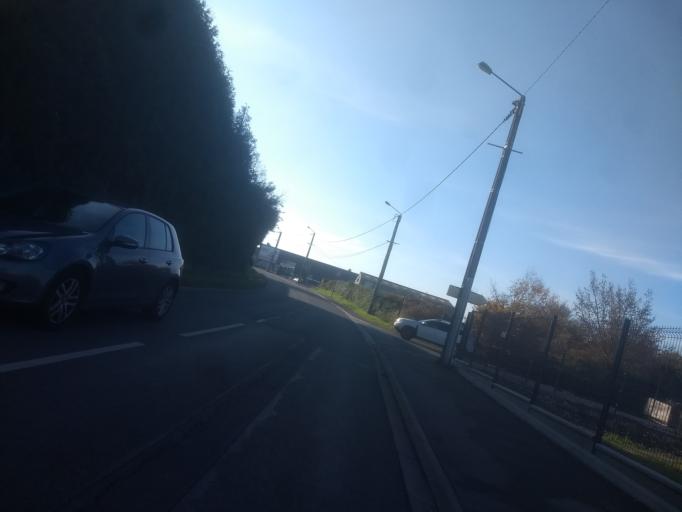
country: FR
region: Nord-Pas-de-Calais
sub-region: Departement du Pas-de-Calais
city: Achicourt
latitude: 50.2768
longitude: 2.7693
